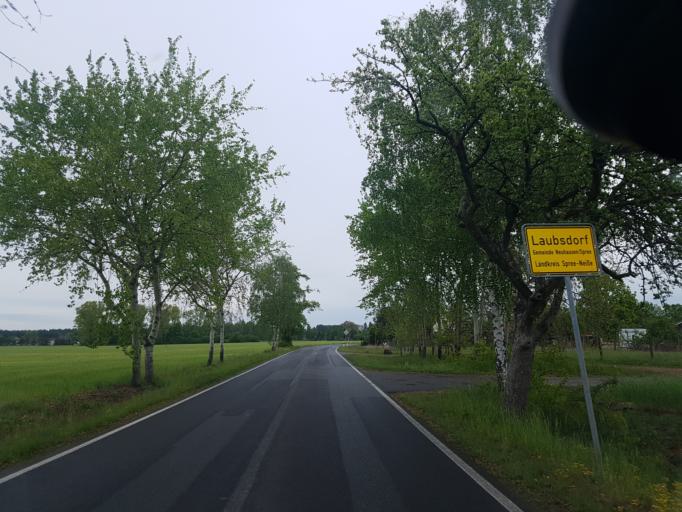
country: DE
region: Brandenburg
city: Spremberg
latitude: 51.6678
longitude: 14.4406
